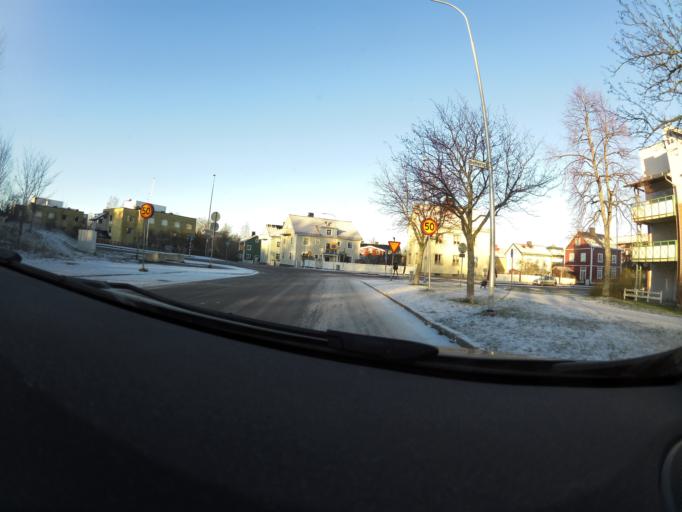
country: SE
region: Gaevleborg
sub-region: Gavle Kommun
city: Gavle
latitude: 60.6656
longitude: 17.1455
